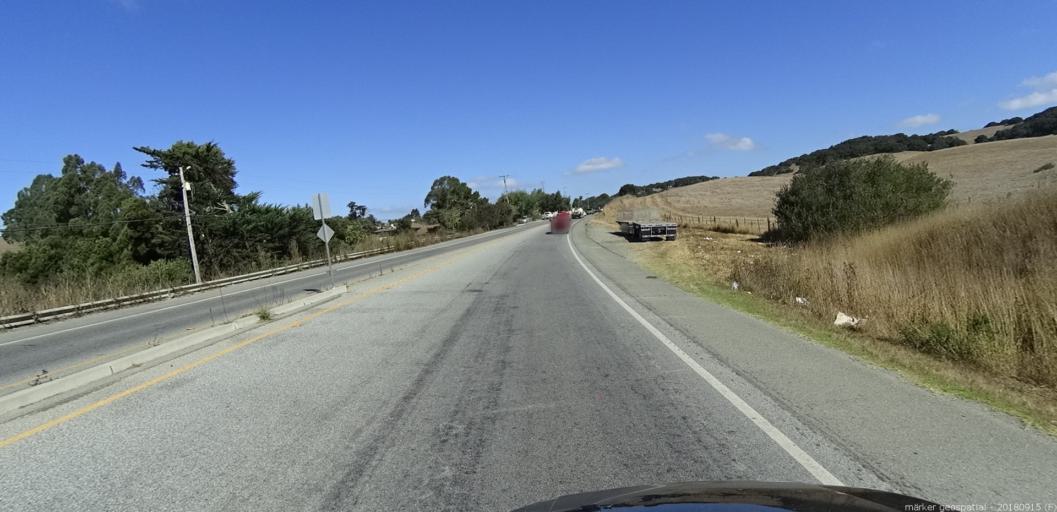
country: US
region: California
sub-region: Monterey County
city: Las Lomas
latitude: 36.8698
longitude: -121.7442
